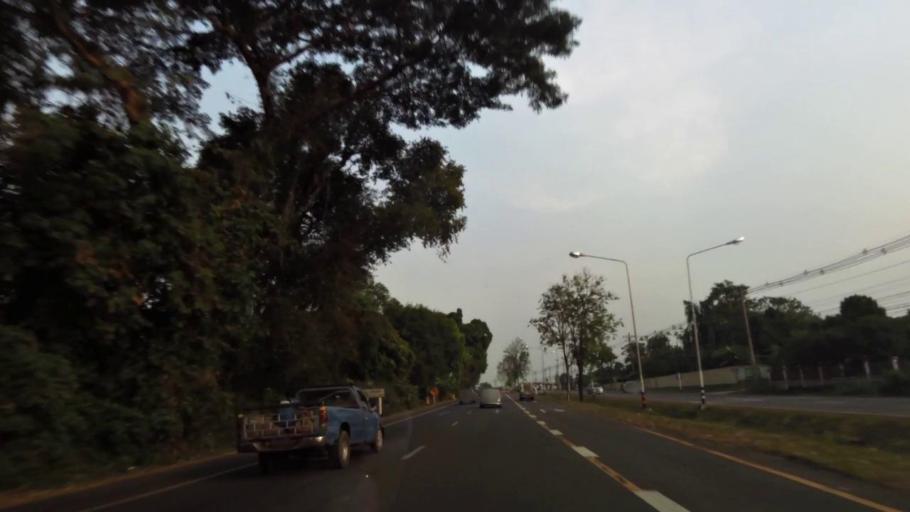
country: TH
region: Chanthaburi
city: Khlung
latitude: 12.4664
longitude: 102.2043
